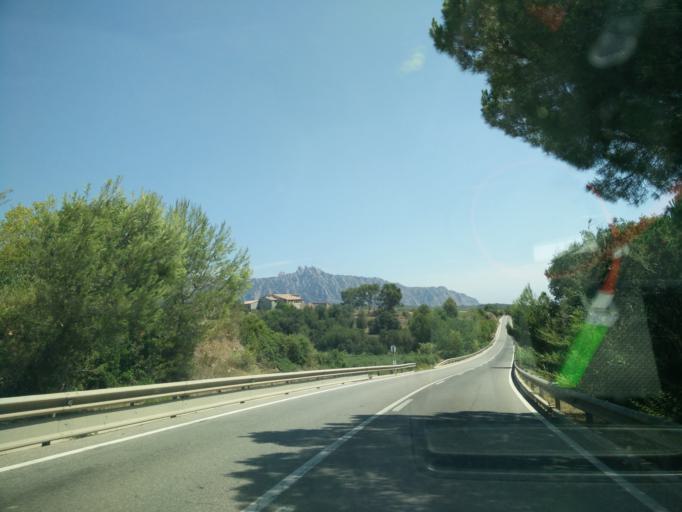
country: ES
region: Catalonia
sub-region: Provincia de Barcelona
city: Piera
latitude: 41.5465
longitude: 1.7619
